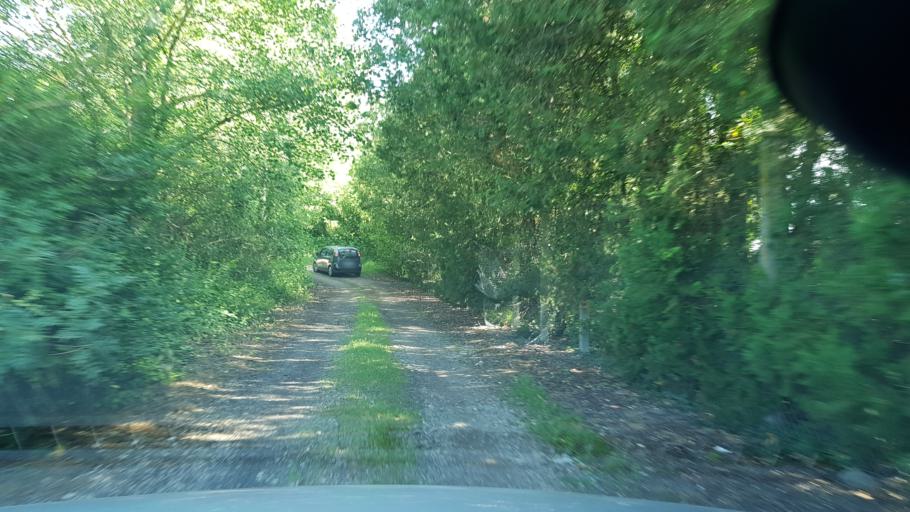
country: FR
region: Centre
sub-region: Departement du Loir-et-Cher
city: Selles-sur-Cher
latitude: 47.2730
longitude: 1.5514
